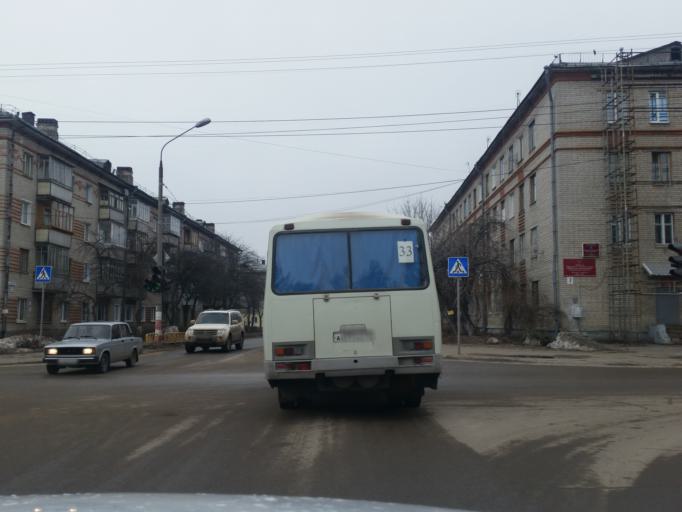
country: RU
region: Ulyanovsk
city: Dimitrovgrad
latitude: 54.2280
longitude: 49.5492
